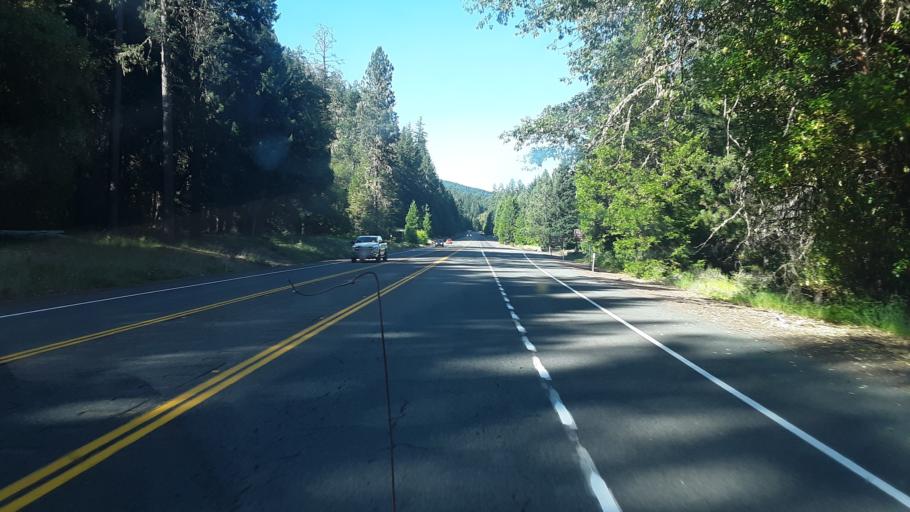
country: US
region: Oregon
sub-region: Jackson County
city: Shady Cove
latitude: 42.6836
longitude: -122.6125
